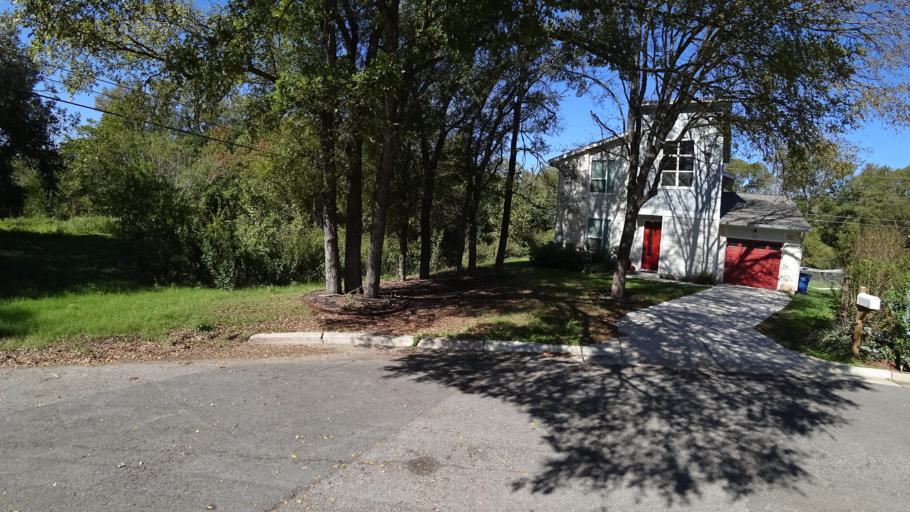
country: US
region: Texas
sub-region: Travis County
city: Austin
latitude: 30.2847
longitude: -97.6780
